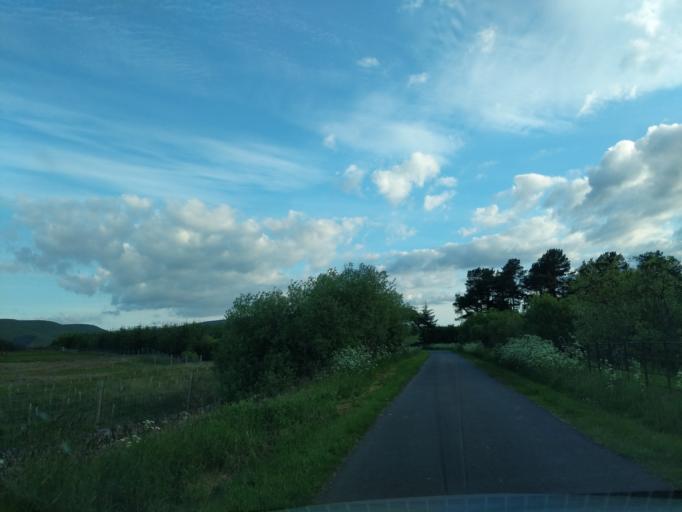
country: GB
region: Scotland
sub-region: Midlothian
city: Gorebridge
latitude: 55.7757
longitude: -3.1034
